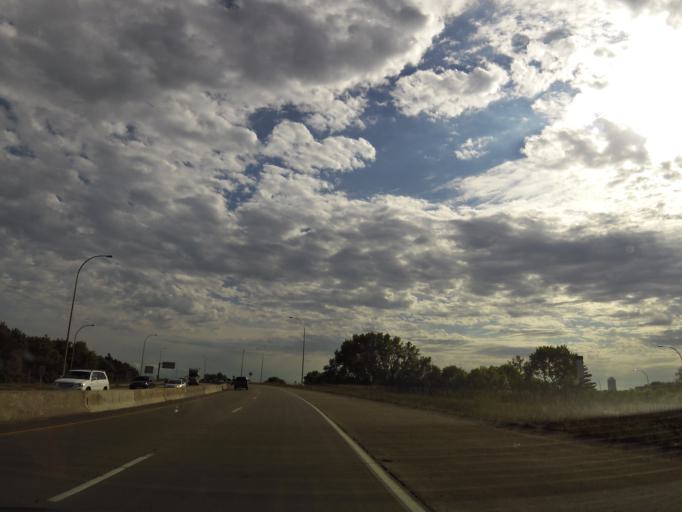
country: US
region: Minnesota
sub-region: Hennepin County
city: Minnetonka Mills
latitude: 44.9257
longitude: -93.4010
